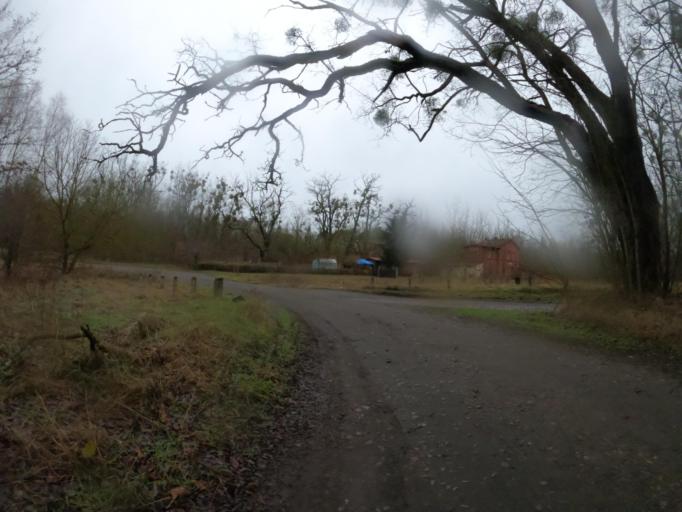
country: PL
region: West Pomeranian Voivodeship
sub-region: Powiat mysliborski
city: Debno
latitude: 52.8021
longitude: 14.7499
